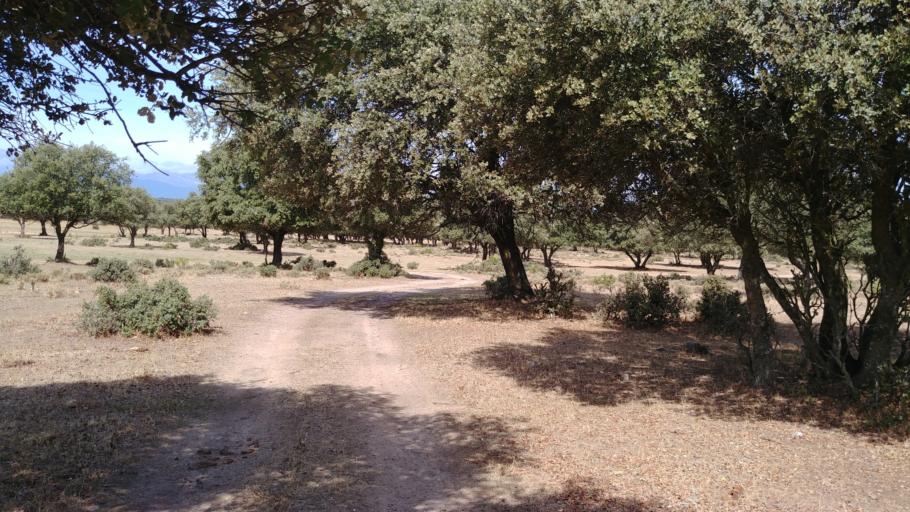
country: ES
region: Castille-La Mancha
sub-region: Province of Toledo
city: Navalcan
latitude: 40.0451
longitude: -5.1131
